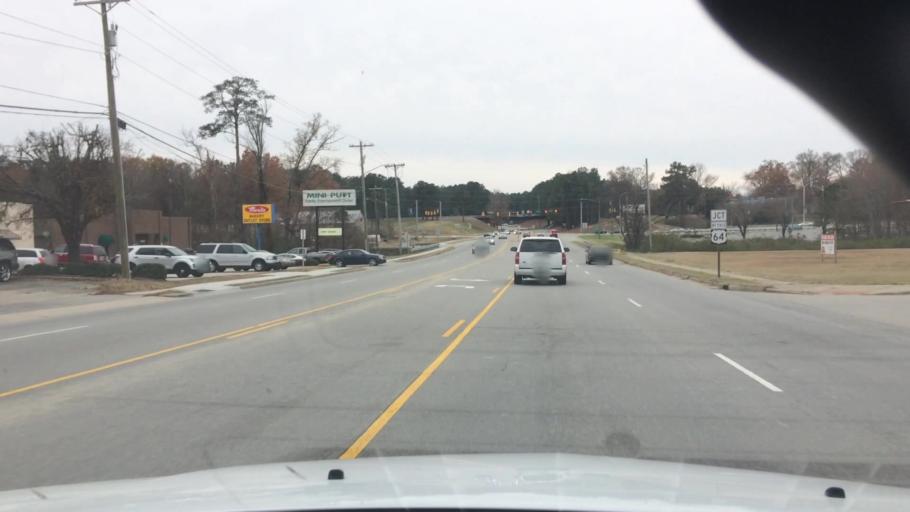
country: US
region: North Carolina
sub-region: Nash County
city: Rocky Mount
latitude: 35.9678
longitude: -77.8026
